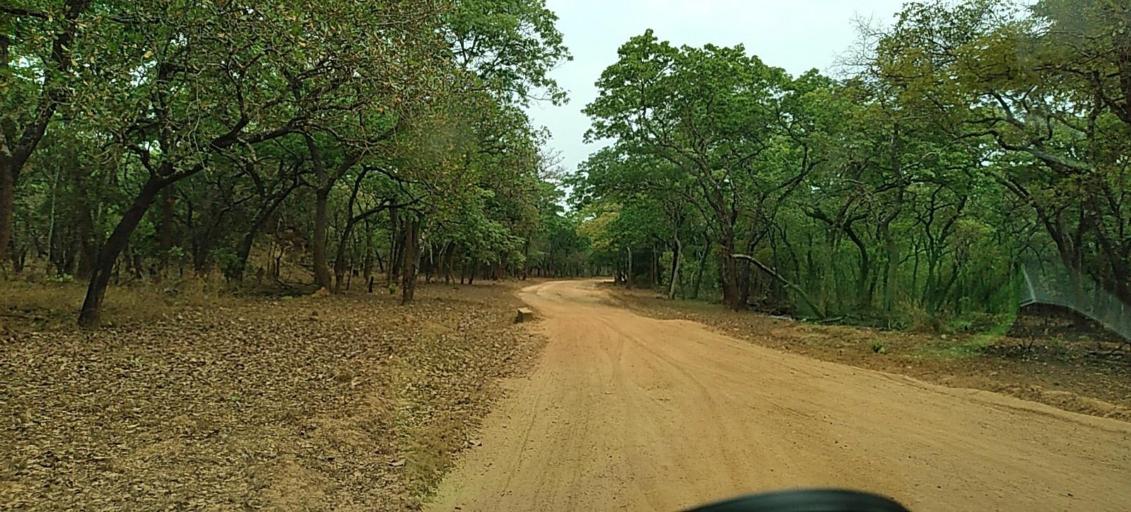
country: ZM
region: North-Western
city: Solwezi
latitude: -12.9168
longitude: 26.5589
